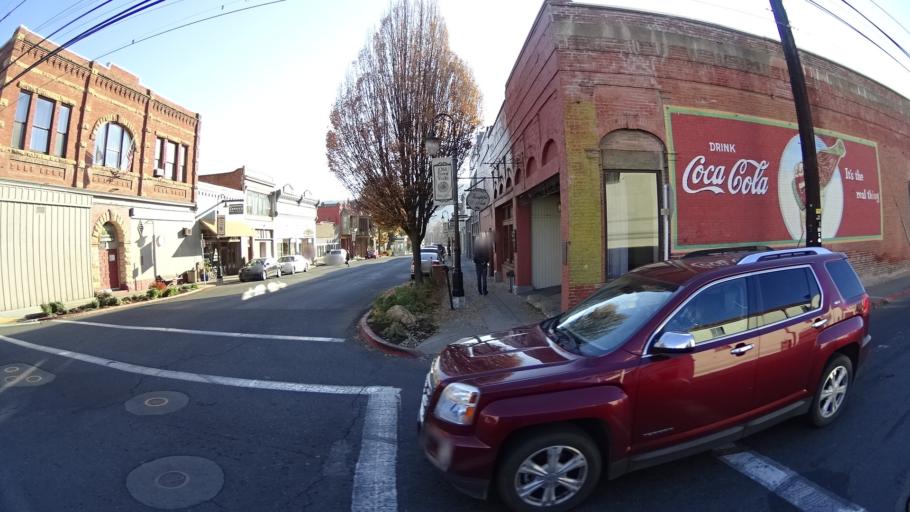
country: US
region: California
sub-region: Siskiyou County
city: Yreka
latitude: 41.7322
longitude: -122.6384
